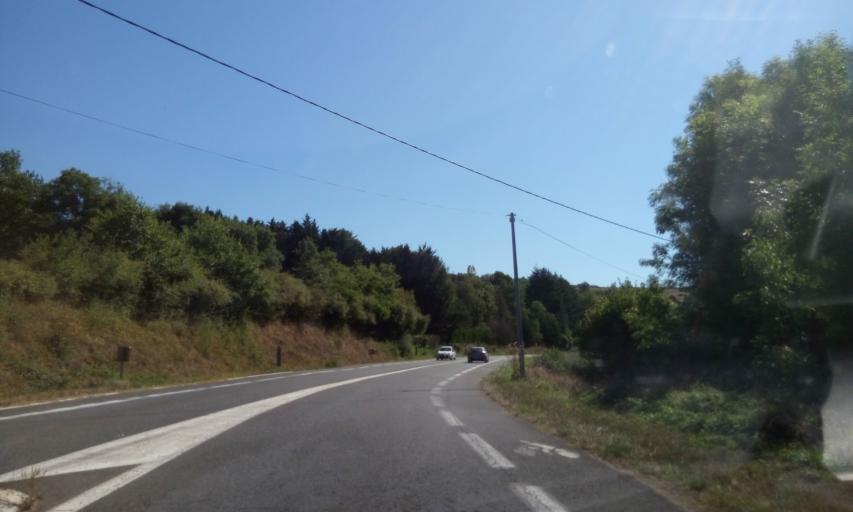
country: FR
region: Rhone-Alpes
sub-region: Departement du Rhone
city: Saint-Verand
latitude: 45.9226
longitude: 4.5635
